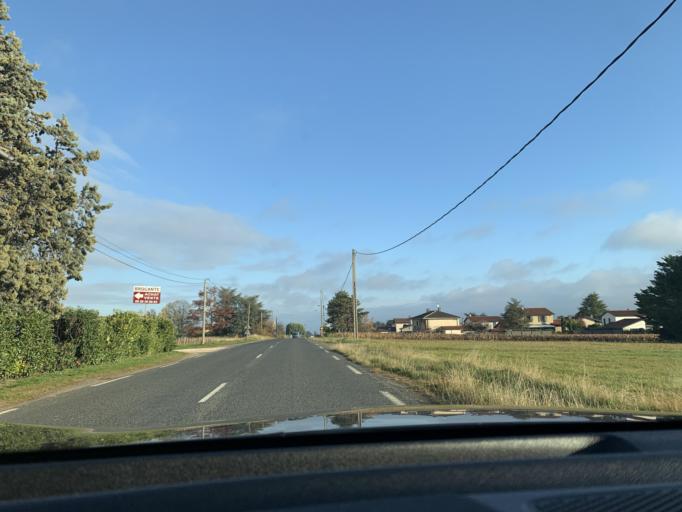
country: FR
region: Rhone-Alpes
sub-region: Departement du Rhone
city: Pommiers
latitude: 45.9476
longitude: 4.6910
